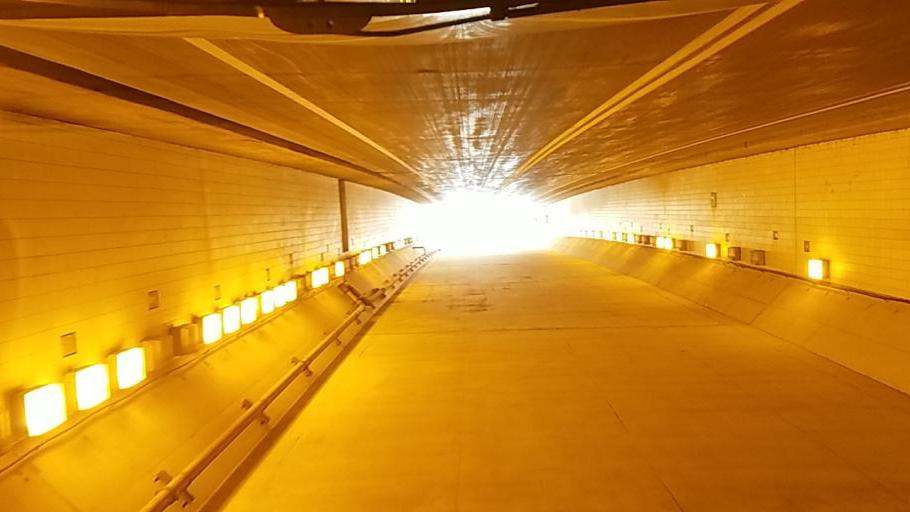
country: US
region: Minnesota
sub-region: Hennepin County
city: Richfield
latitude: 44.8835
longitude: -93.2370
